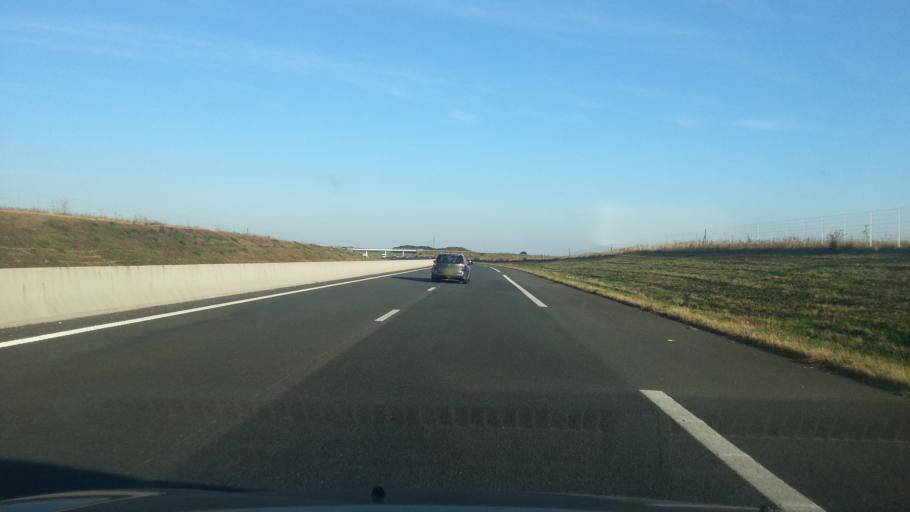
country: FR
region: Picardie
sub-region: Departement de l'Oise
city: Catenoy
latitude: 49.3828
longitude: 2.5060
